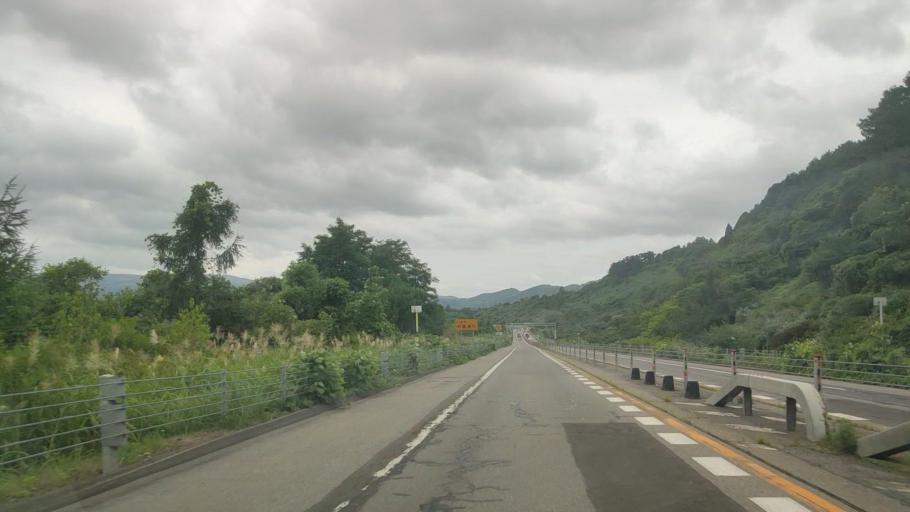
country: JP
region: Hokkaido
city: Nanae
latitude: 41.9094
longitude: 140.6945
